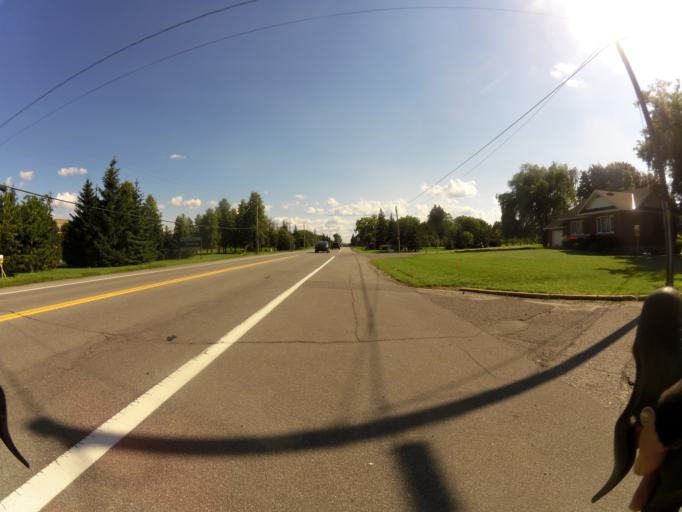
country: CA
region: Ontario
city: Ottawa
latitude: 45.3175
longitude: -75.6918
